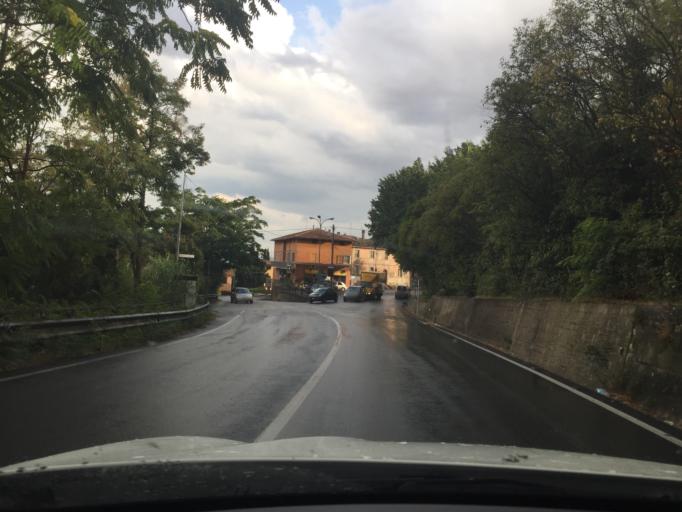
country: IT
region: Umbria
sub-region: Provincia di Perugia
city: San Martino in Campo
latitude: 43.0706
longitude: 12.3981
